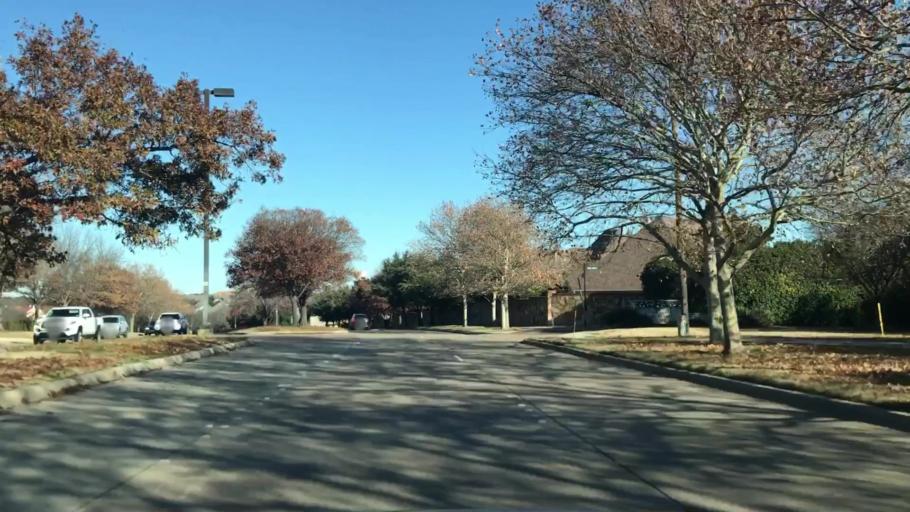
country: US
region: Texas
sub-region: Denton County
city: The Colony
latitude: 33.0906
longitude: -96.8392
